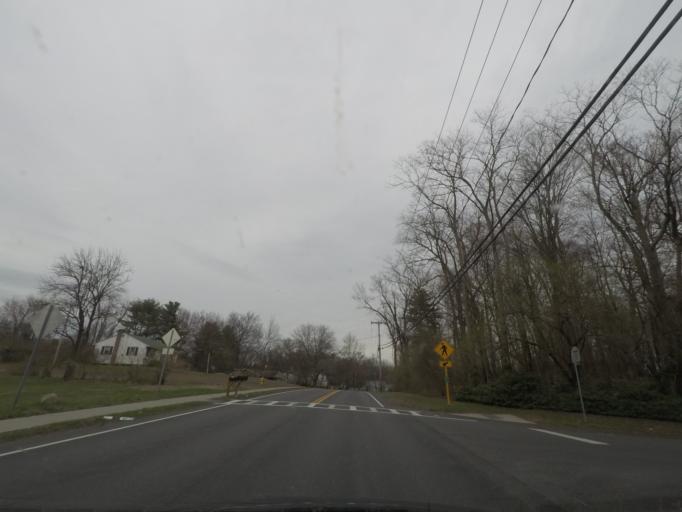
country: US
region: New York
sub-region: Albany County
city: Delmar
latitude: 42.6023
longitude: -73.8106
